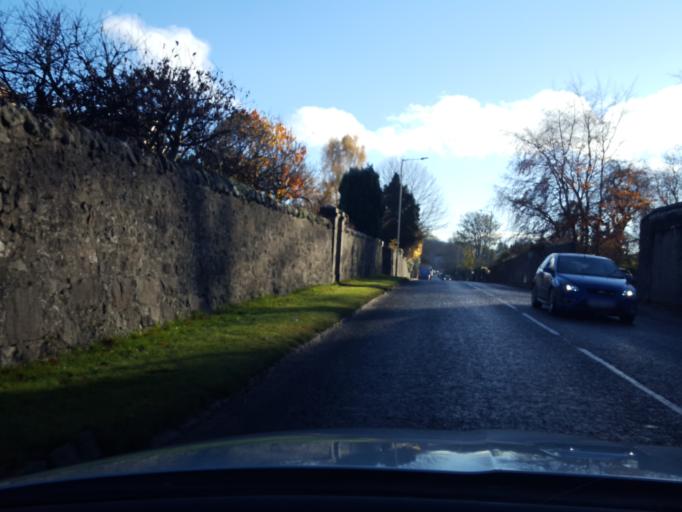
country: GB
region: Scotland
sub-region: Perth and Kinross
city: Perth
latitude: 56.4047
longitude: -3.4250
